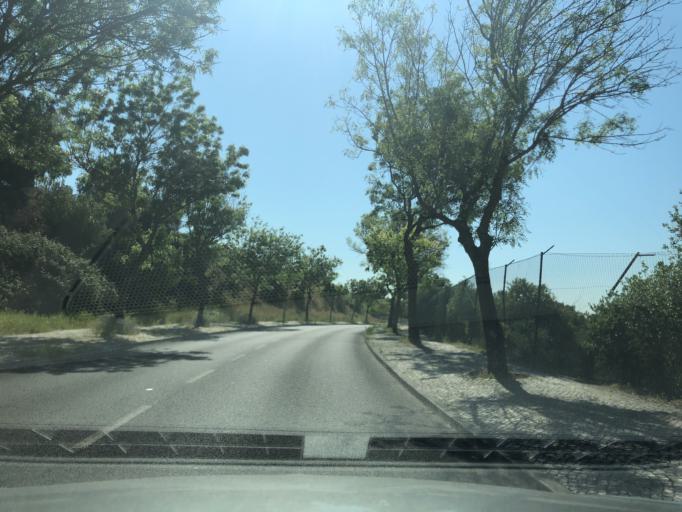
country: PT
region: Lisbon
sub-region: Oeiras
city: Carnaxide
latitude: 38.7324
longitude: -9.2458
